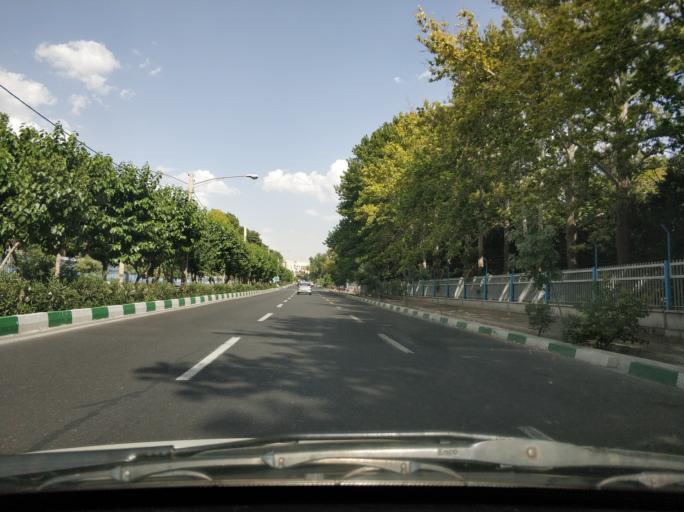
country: IR
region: Tehran
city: Tehran
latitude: 35.7432
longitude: 51.5824
